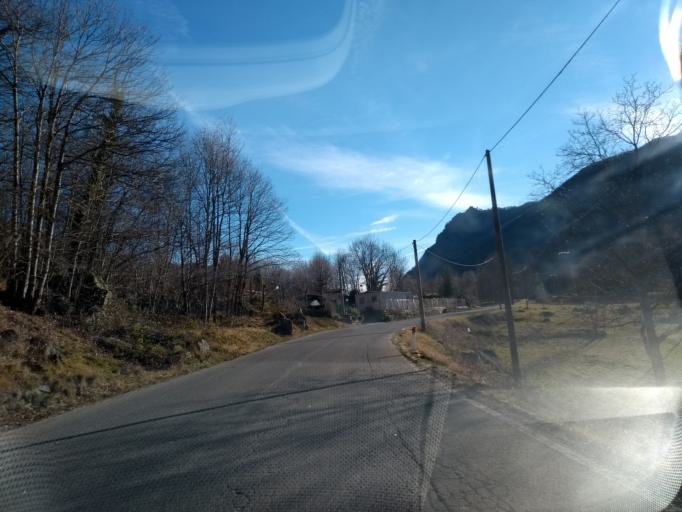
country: IT
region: Piedmont
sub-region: Provincia di Torino
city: Cantoira
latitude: 45.3501
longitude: 7.3703
